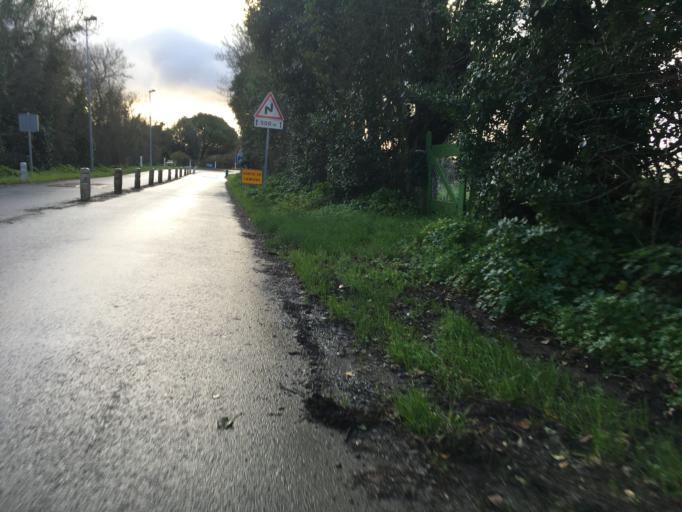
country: FR
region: Poitou-Charentes
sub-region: Departement de la Charente-Maritime
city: Nieul-sur-Mer
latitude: 46.1899
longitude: -1.1831
